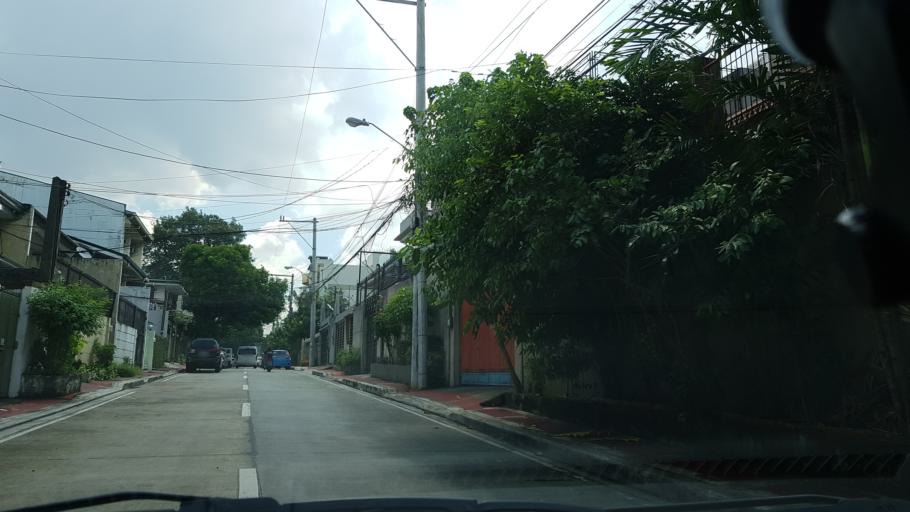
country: PH
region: Calabarzon
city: Del Monte
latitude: 14.6319
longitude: 121.0238
